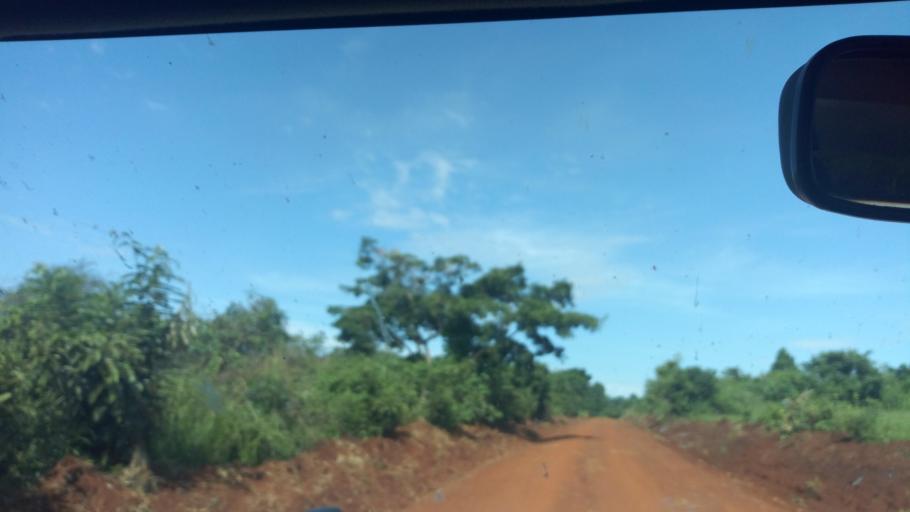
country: UG
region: Western Region
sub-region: Masindi District
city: Masindi
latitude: 1.6453
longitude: 31.7742
